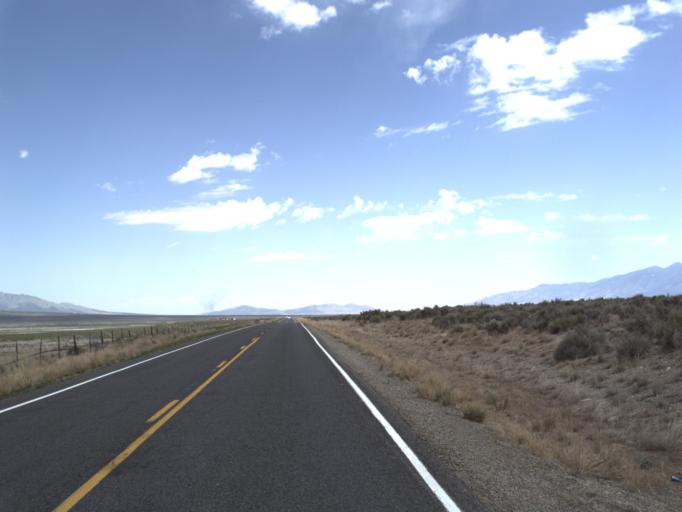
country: US
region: Utah
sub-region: Tooele County
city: Tooele
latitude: 40.1047
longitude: -112.4308
